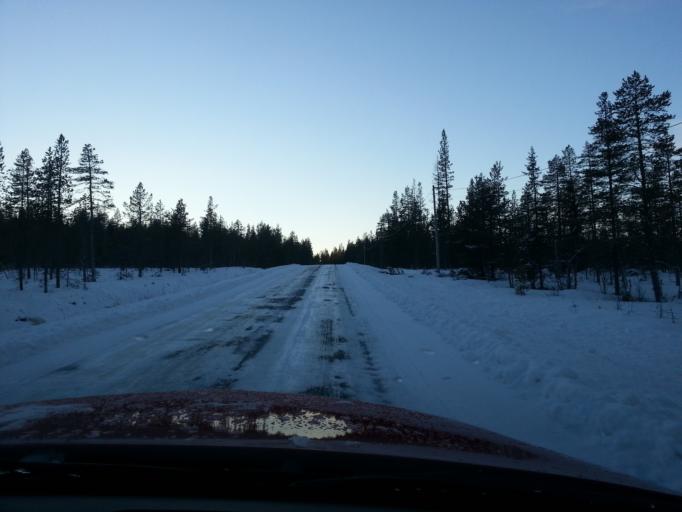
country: SE
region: Jaemtland
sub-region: Harjedalens Kommun
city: Sveg
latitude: 62.3579
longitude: 13.4512
